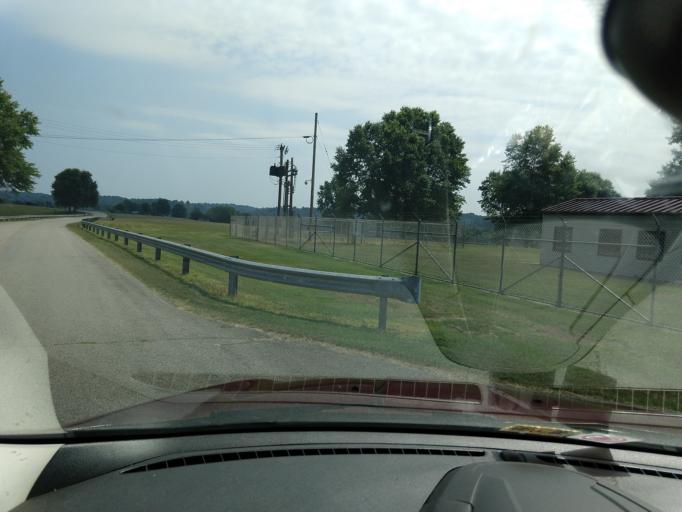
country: US
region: West Virginia
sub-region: Mason County
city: New Haven
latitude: 38.9195
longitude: -81.9129
